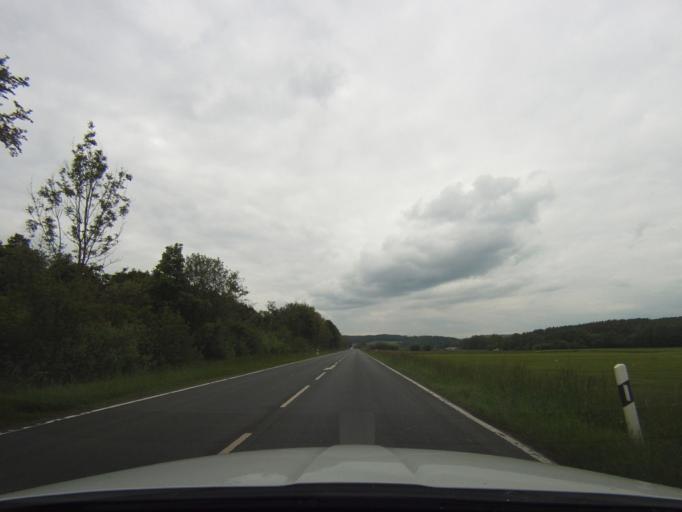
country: DE
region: Bavaria
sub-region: Upper Franconia
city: Weismain
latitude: 50.1050
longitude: 11.2362
